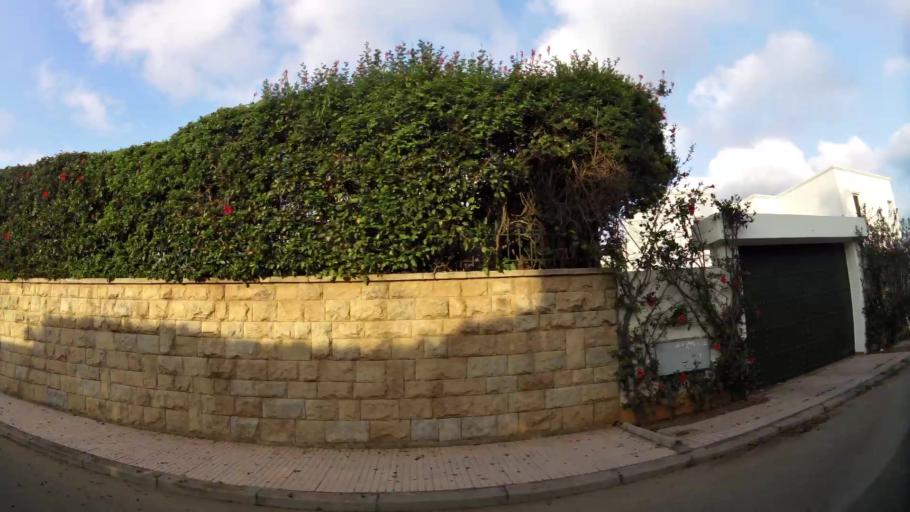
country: MA
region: Rabat-Sale-Zemmour-Zaer
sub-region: Rabat
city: Rabat
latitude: 33.9595
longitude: -6.8308
